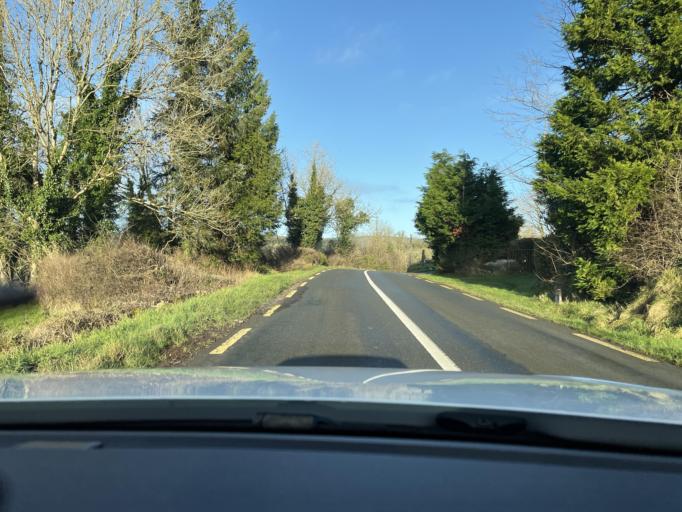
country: IE
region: Connaught
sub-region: County Leitrim
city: Manorhamilton
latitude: 54.1740
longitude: -8.1135
